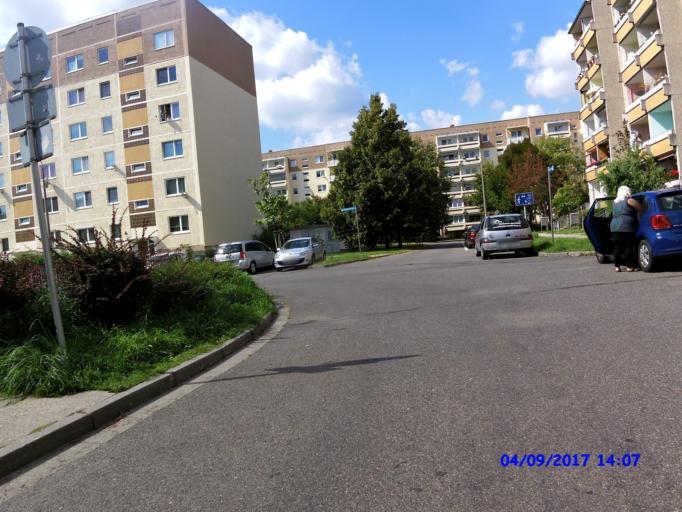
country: DE
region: Saxony
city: Taucha
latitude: 51.3515
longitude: 12.4626
